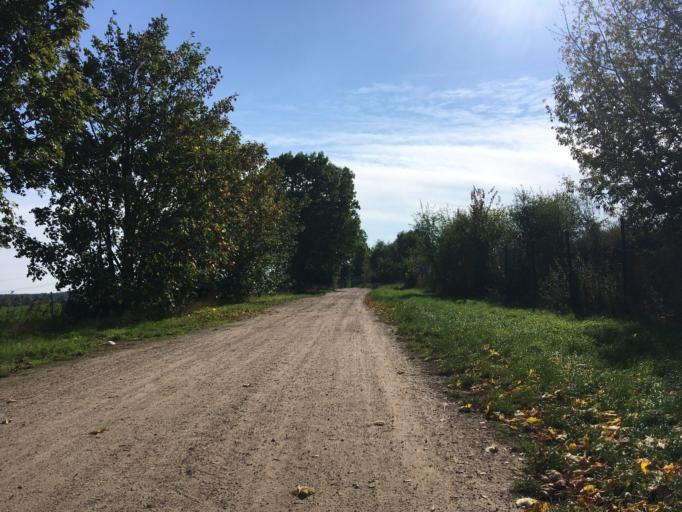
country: DE
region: Brandenburg
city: Altlandsberg
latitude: 52.5511
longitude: 13.7261
